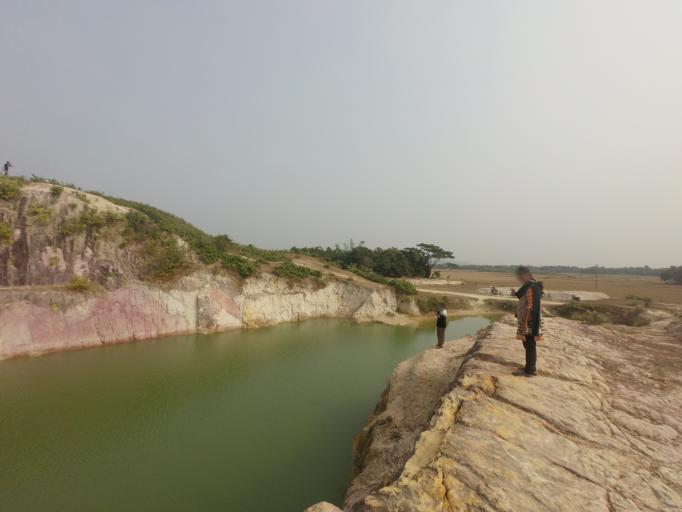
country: BD
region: Dhaka
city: Netrakona
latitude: 25.1575
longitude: 90.6432
